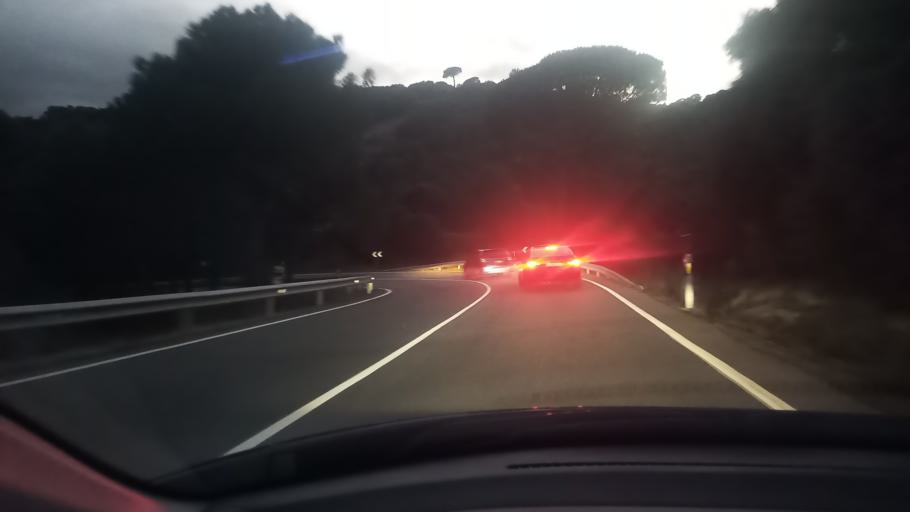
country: ES
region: Madrid
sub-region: Provincia de Madrid
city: Navas del Rey
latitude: 40.4403
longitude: -4.2661
